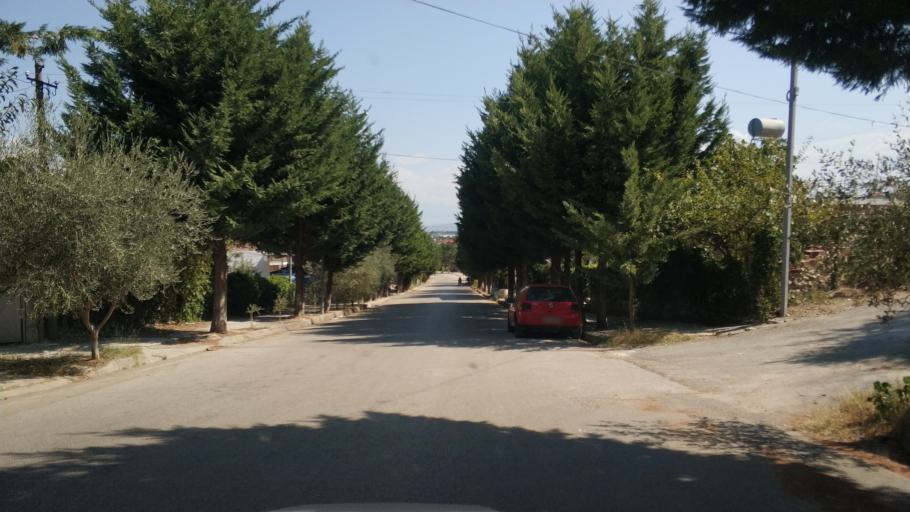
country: AL
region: Fier
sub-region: Rrethi i Lushnjes
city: Kolonje
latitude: 40.8265
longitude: 19.6034
